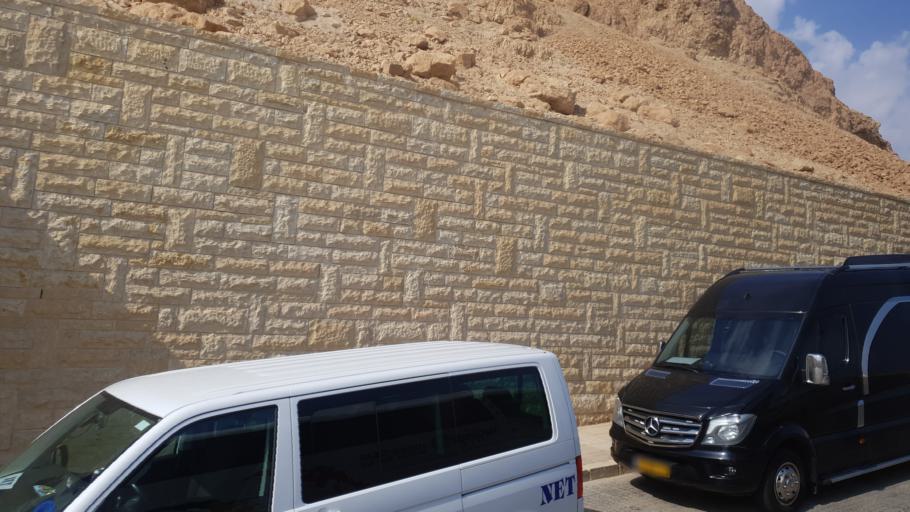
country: IL
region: Southern District
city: `En Boqeq
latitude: 31.3106
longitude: 35.3625
